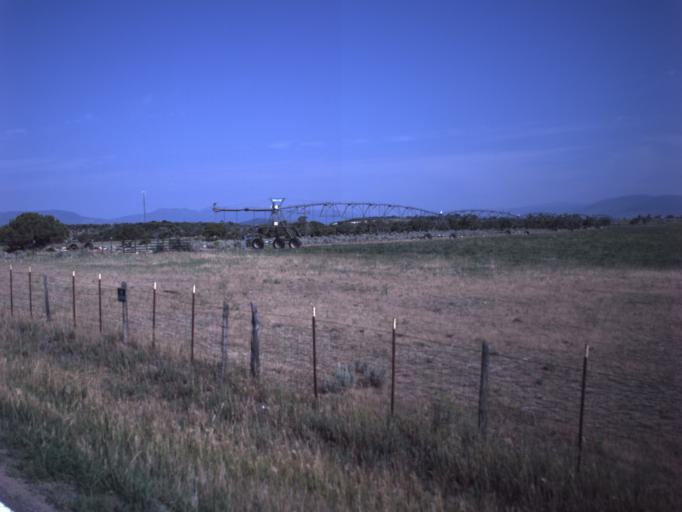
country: US
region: Utah
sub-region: Duchesne County
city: Duchesne
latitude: 40.3555
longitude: -110.3733
